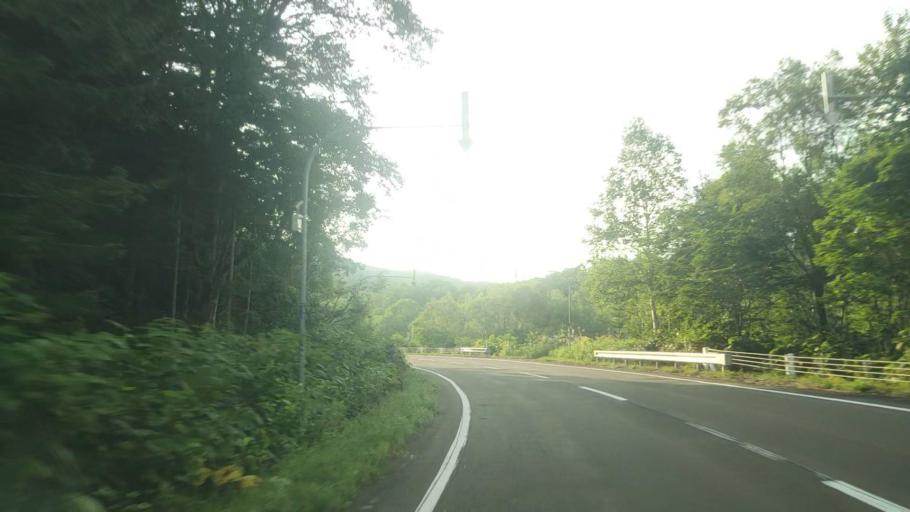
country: JP
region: Hokkaido
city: Bibai
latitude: 43.1287
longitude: 142.1013
